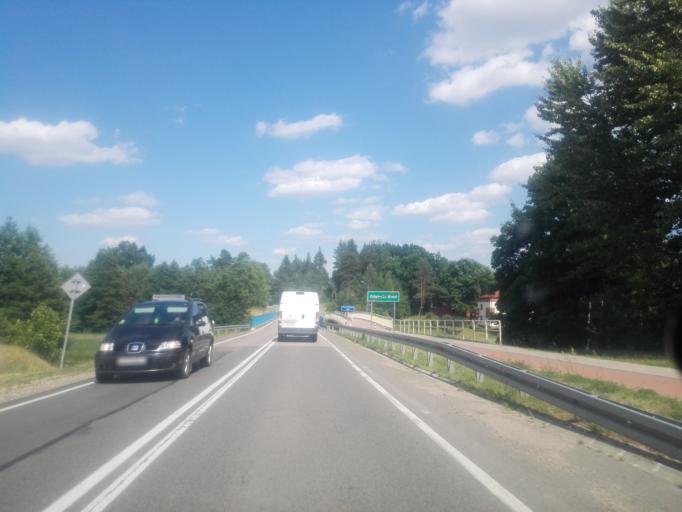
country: PL
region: Podlasie
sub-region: Powiat sejnenski
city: Sejny
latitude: 53.9793
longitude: 23.2891
